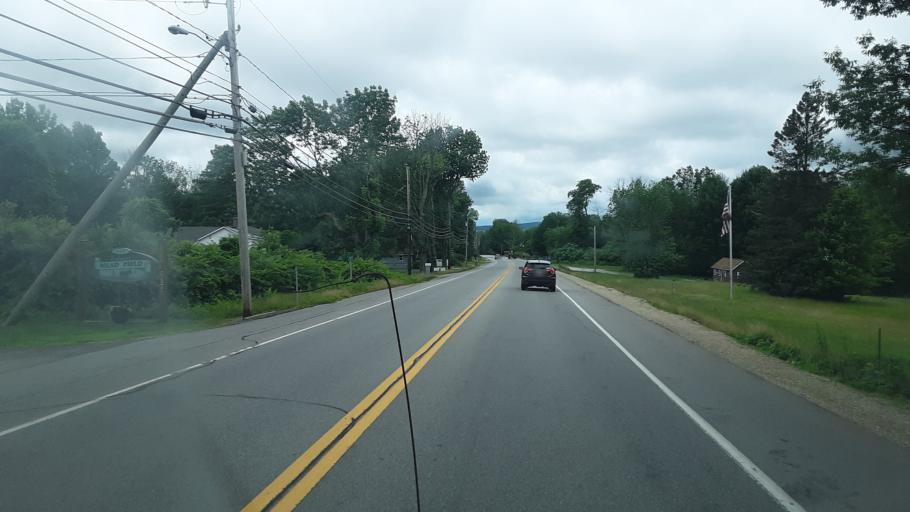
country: US
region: New Hampshire
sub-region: Rockingham County
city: Northwood
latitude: 43.2097
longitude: -71.1865
